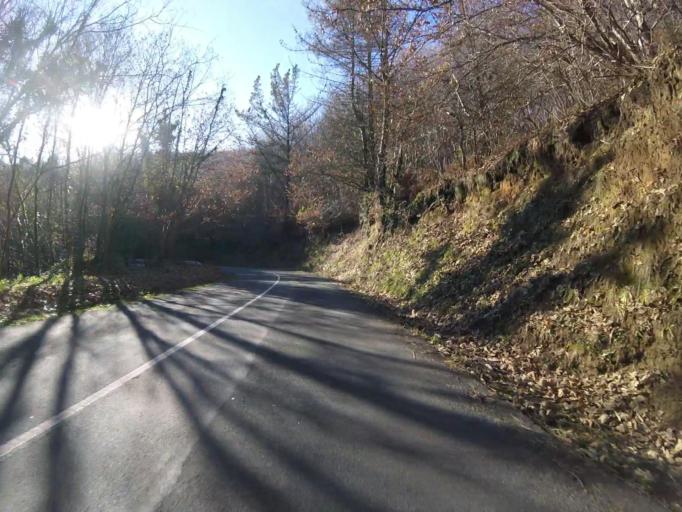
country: ES
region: Basque Country
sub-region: Provincia de Guipuzcoa
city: Fuenterrabia
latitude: 43.3679
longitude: -1.8273
